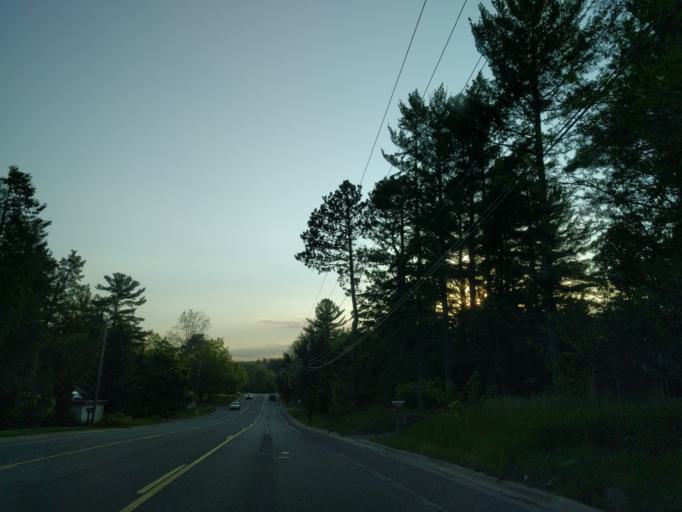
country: US
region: Michigan
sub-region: Marquette County
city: Trowbridge Park
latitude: 46.5642
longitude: -87.4277
